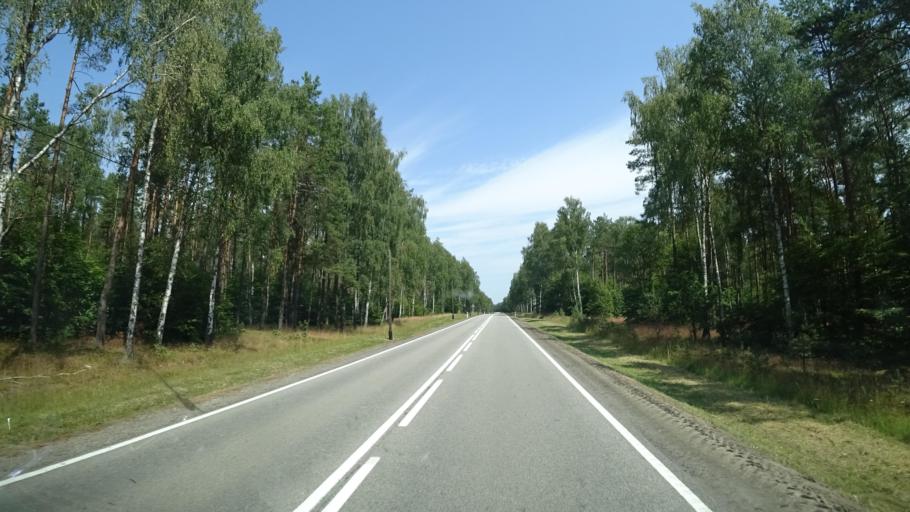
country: PL
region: Pomeranian Voivodeship
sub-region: Powiat koscierski
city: Grabowo Koscierskie
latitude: 54.1776
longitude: 18.0825
